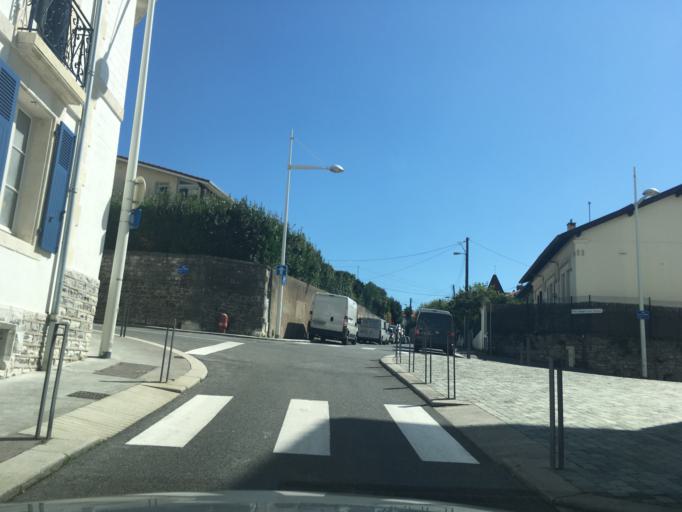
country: FR
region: Aquitaine
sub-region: Departement des Pyrenees-Atlantiques
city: Biarritz
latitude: 43.4809
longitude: -1.5536
